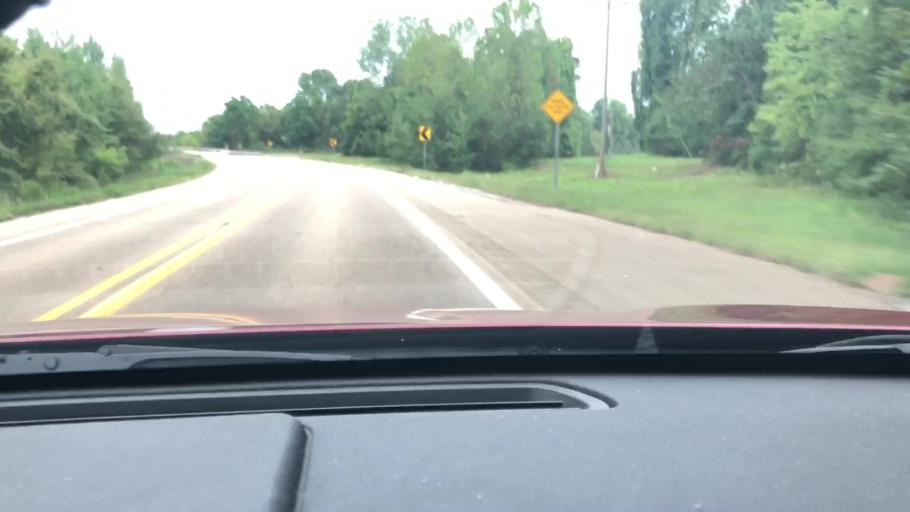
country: US
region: Arkansas
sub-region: Miller County
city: Texarkana
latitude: 33.4143
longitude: -93.8097
